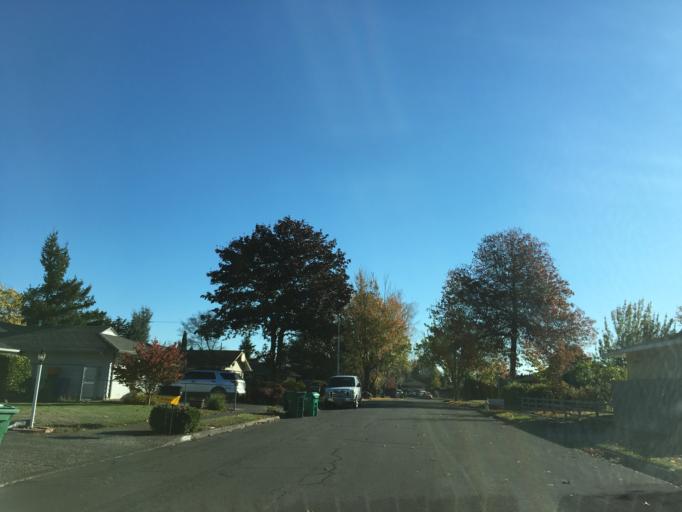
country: US
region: Oregon
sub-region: Multnomah County
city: Wood Village
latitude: 45.5200
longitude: -122.4160
